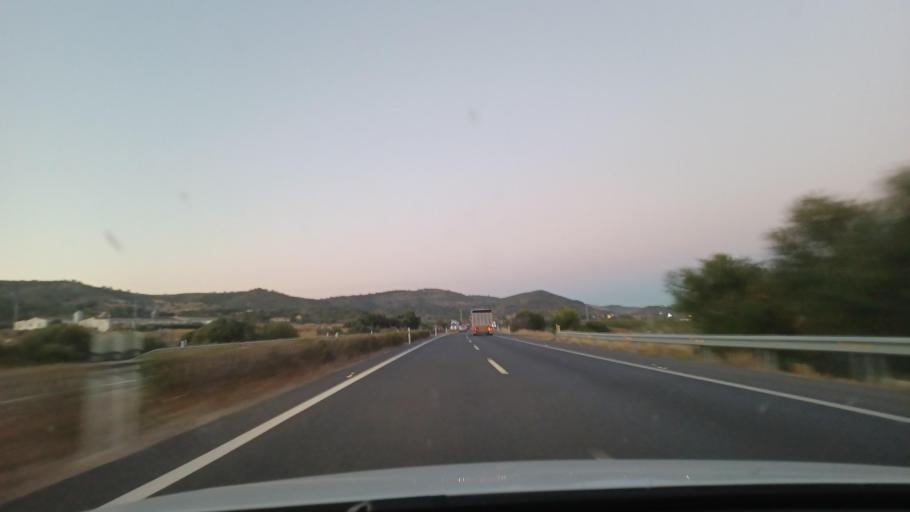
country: ES
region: Valencia
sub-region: Provincia de Castello
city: Torreblanca
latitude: 40.2013
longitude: 0.1755
